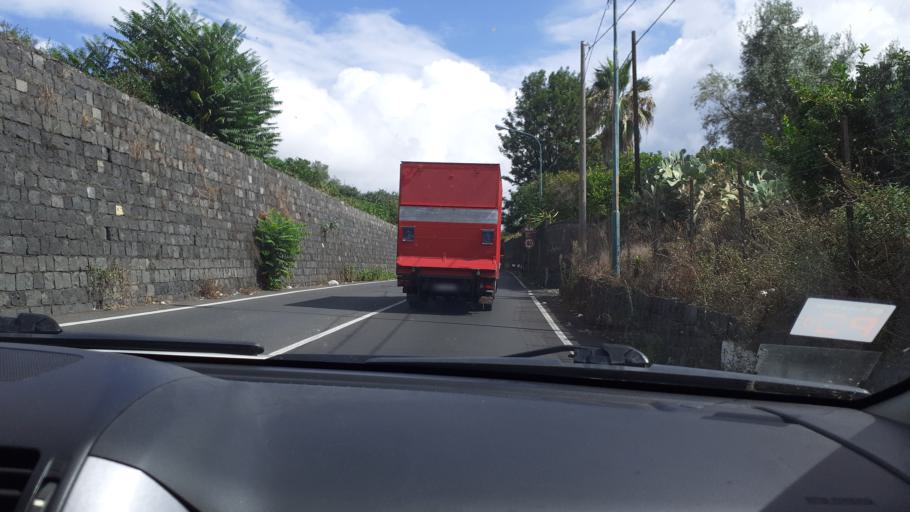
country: IT
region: Sicily
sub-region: Catania
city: Canalicchio
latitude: 37.5455
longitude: 15.0998
